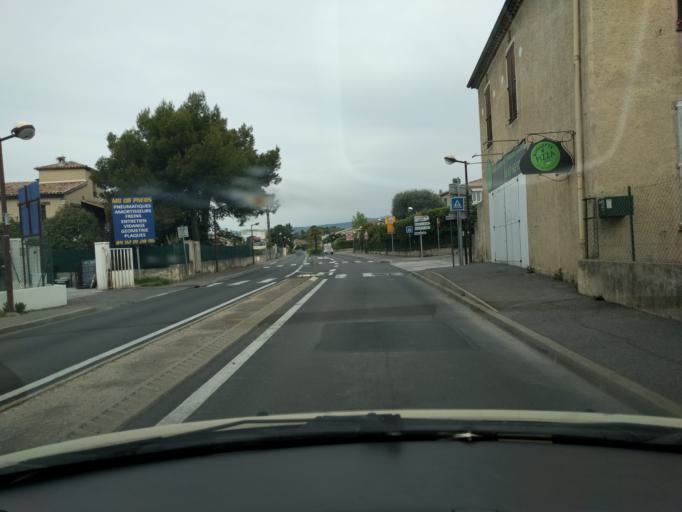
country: FR
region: Provence-Alpes-Cote d'Azur
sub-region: Departement des Alpes-Maritimes
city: La Roquette-sur-Siagne
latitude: 43.5786
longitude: 6.9500
